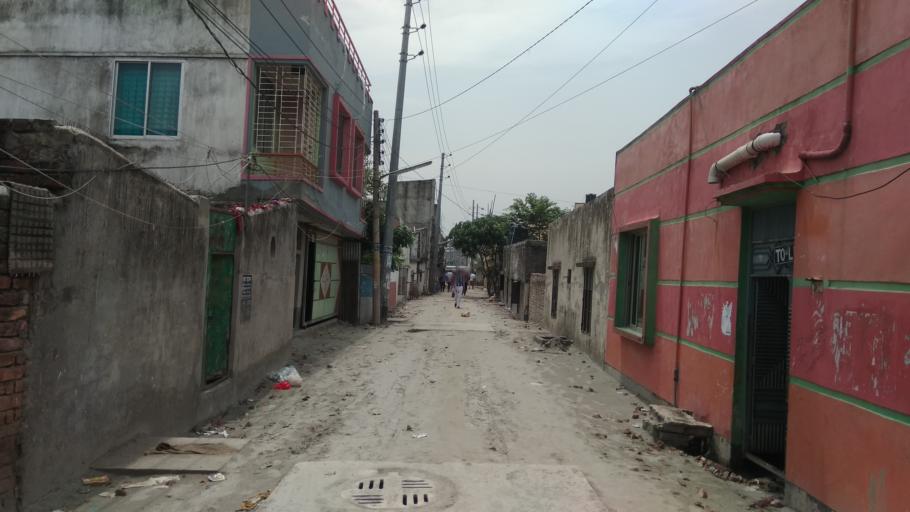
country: BD
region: Dhaka
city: Tungi
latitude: 23.8163
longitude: 90.3802
